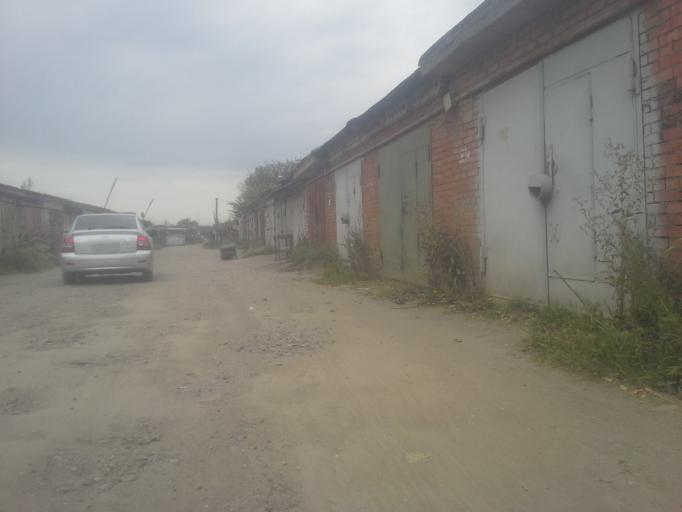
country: RU
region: Moskovskaya
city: Kievskij
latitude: 55.4236
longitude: 36.8716
